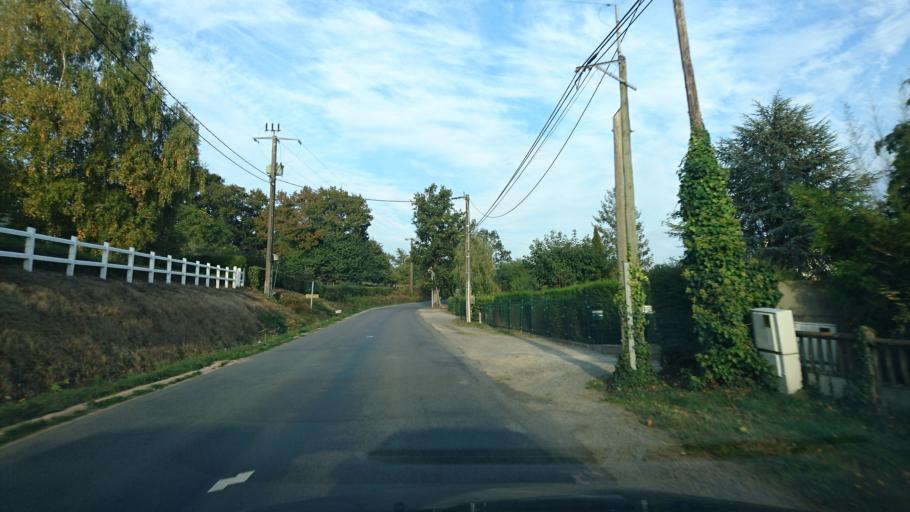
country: FR
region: Pays de la Loire
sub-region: Departement de la Loire-Atlantique
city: Saint-Nicolas-de-Redon
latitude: 47.6750
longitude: -2.0452
